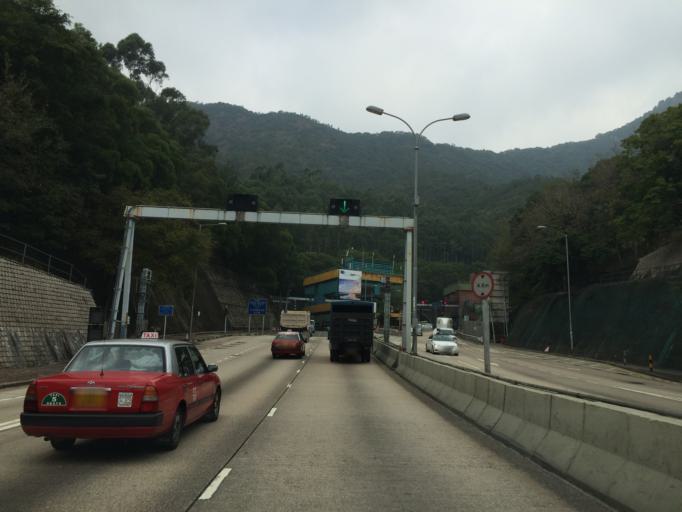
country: HK
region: Wong Tai Sin
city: Wong Tai Sin
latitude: 22.3448
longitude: 114.1815
